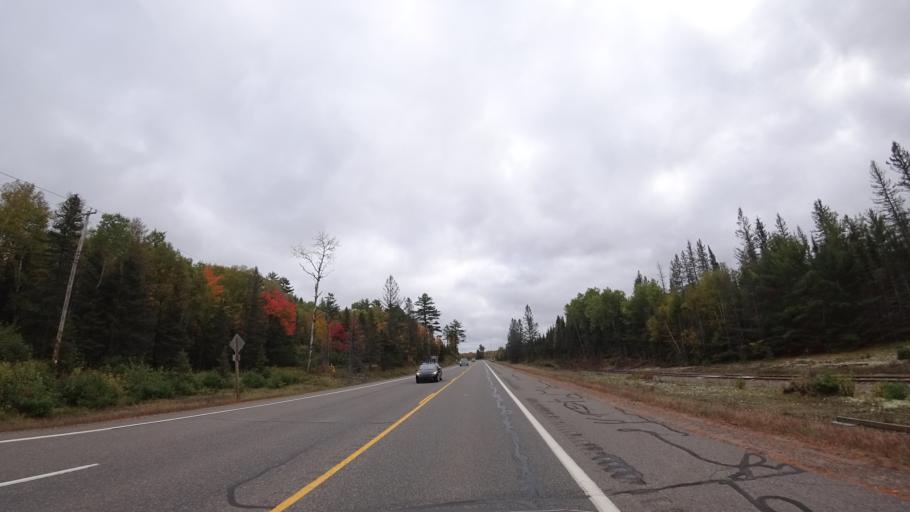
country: US
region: Michigan
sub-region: Marquette County
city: West Ishpeming
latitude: 46.5210
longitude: -87.9833
